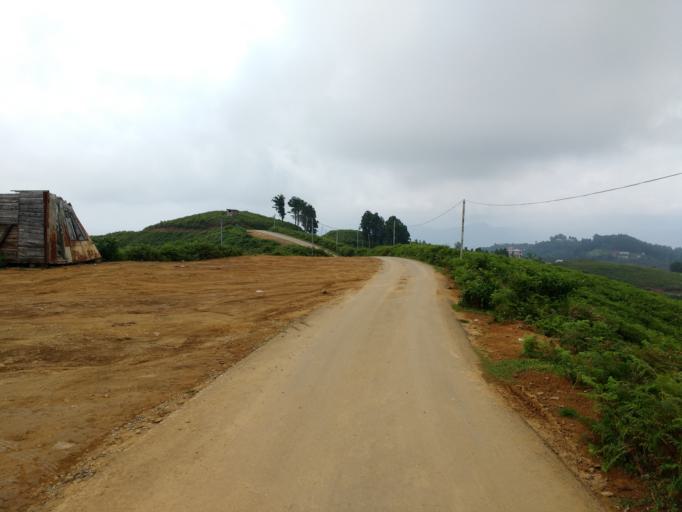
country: GE
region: Ajaria
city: Khelvachauri
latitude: 41.5638
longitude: 41.5837
